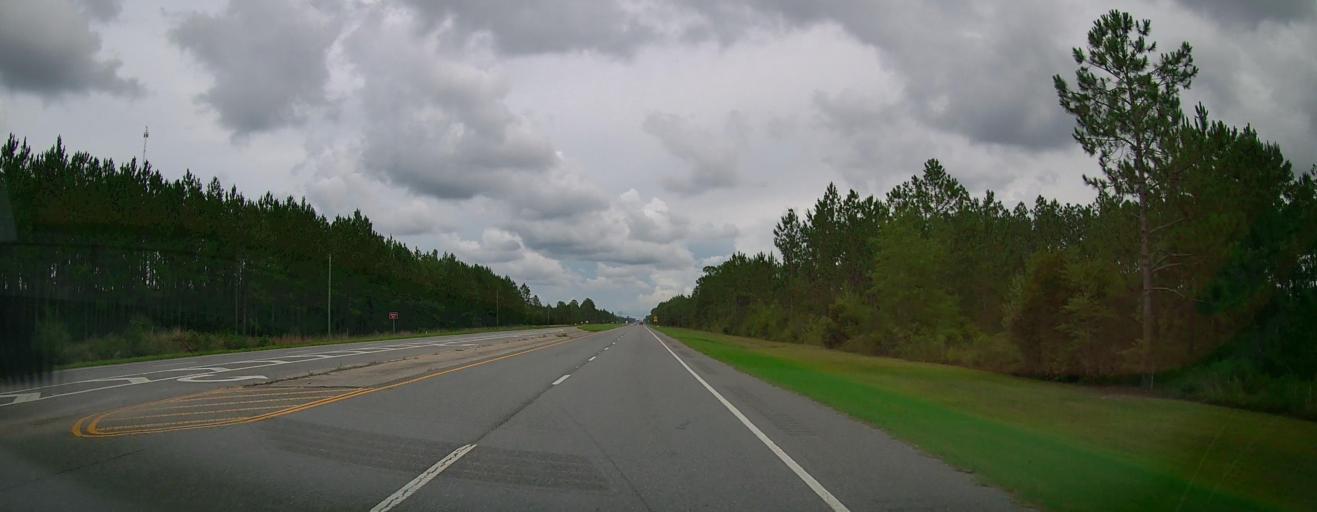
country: US
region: Georgia
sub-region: Wayne County
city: Jesup
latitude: 31.6849
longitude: -82.1059
